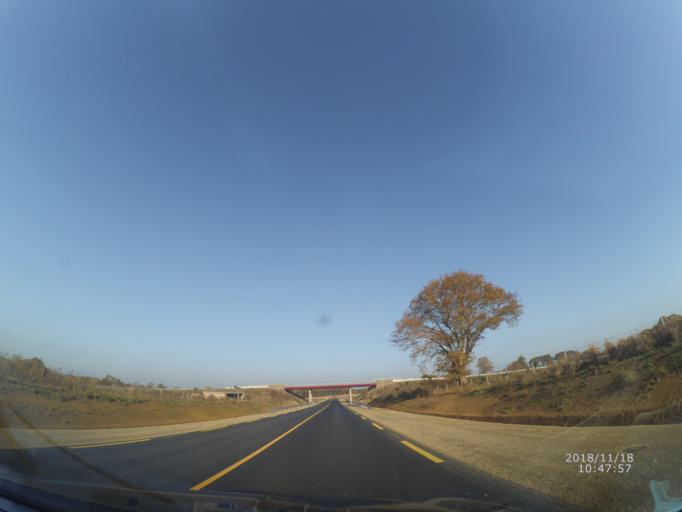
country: FR
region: Pays de la Loire
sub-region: Departement de la Loire-Atlantique
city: Vue
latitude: 47.1988
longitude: -1.9176
